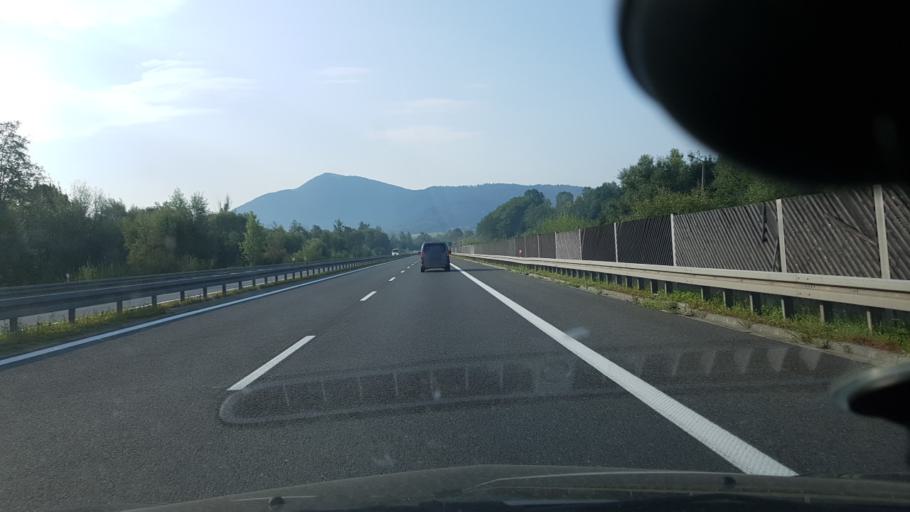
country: PL
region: Lesser Poland Voivodeship
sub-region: Powiat myslenicki
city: Lubien
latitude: 49.7328
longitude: 19.9758
